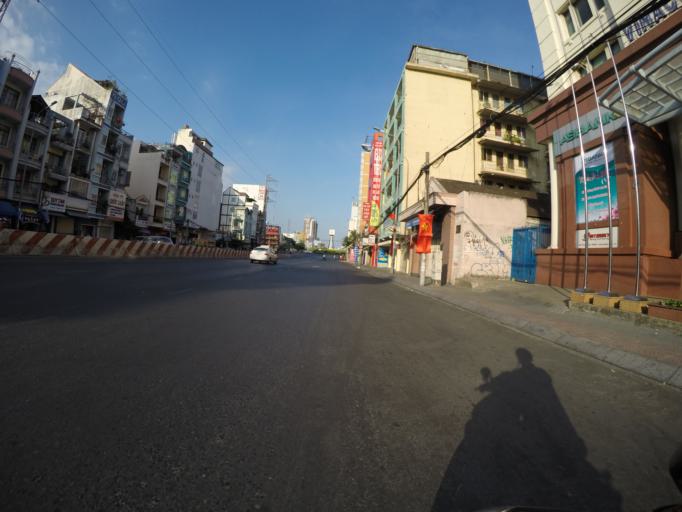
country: VN
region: Ho Chi Minh City
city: Quan Mot
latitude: 10.7911
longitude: 106.6982
